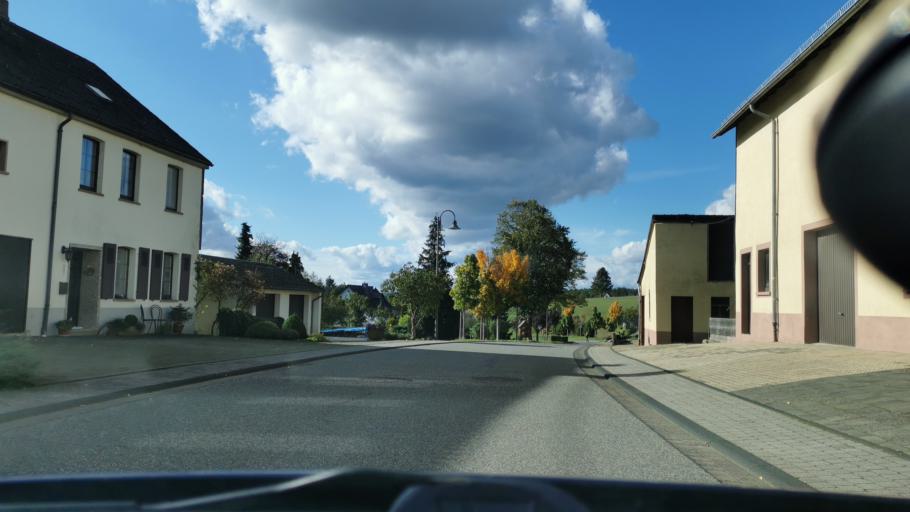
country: DE
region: Rheinland-Pfalz
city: Hupperath
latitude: 49.9968
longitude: 6.8319
